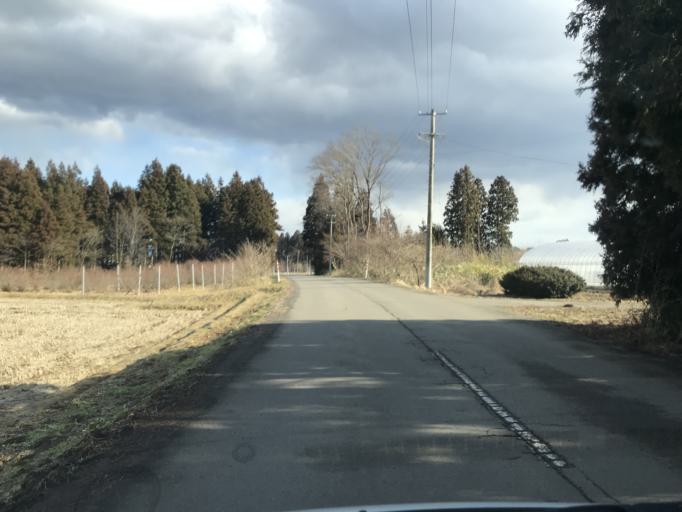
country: JP
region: Iwate
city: Mizusawa
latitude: 39.0984
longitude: 141.0301
